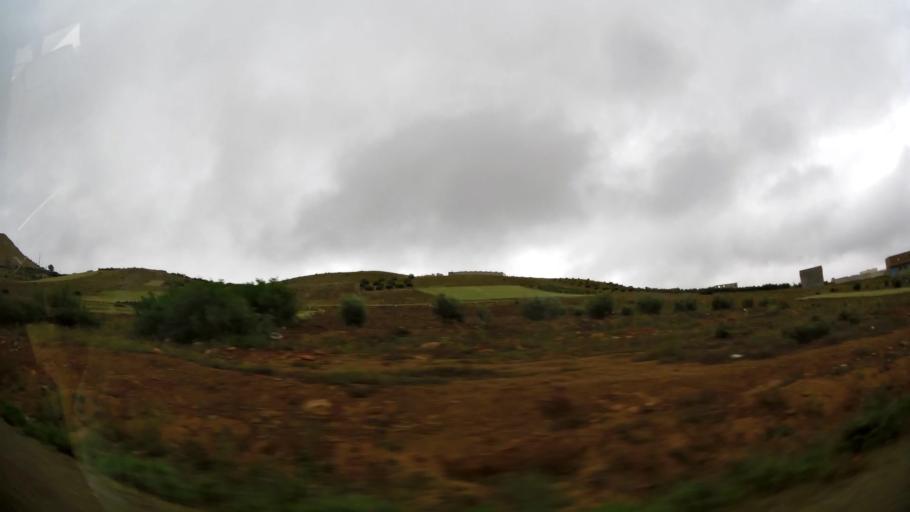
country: MA
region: Oriental
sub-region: Nador
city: Midar
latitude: 35.0613
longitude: -3.4687
